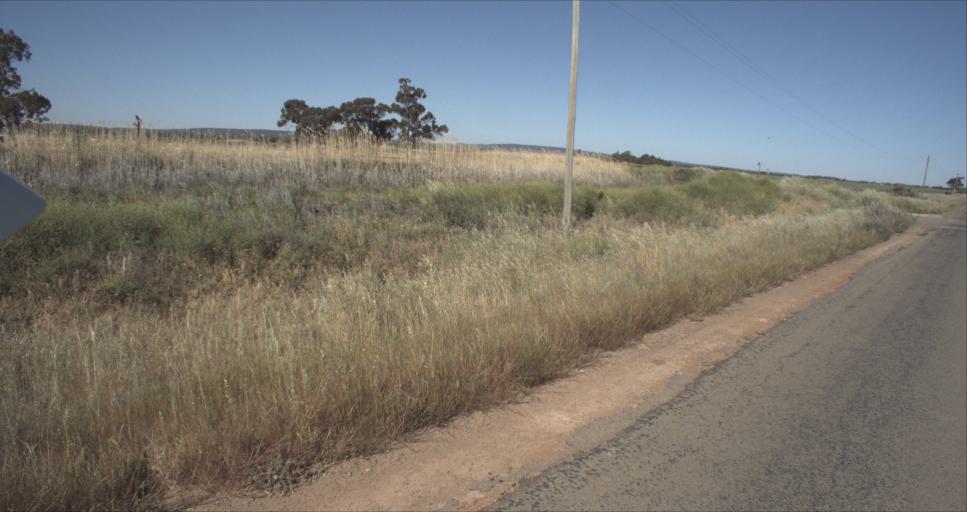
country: AU
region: New South Wales
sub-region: Leeton
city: Leeton
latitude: -34.4798
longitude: 146.3699
